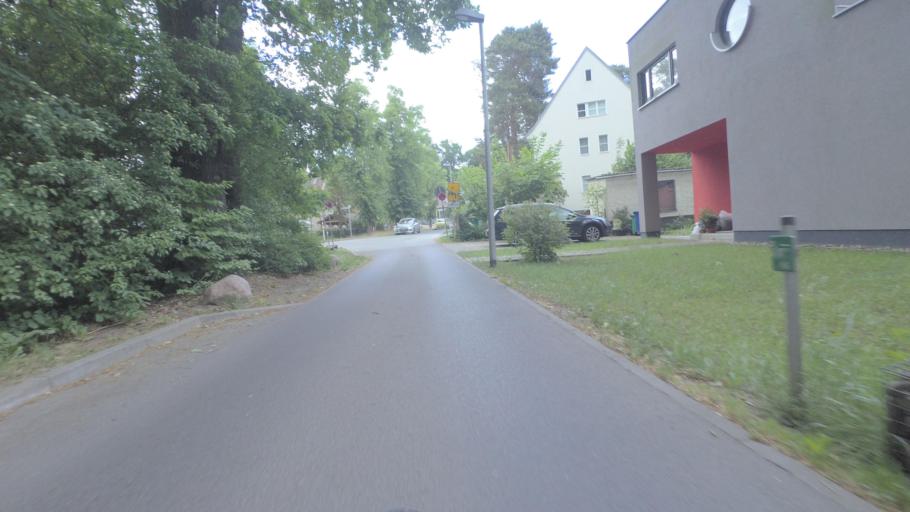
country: DE
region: Brandenburg
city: Rangsdorf
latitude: 52.2897
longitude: 13.4381
